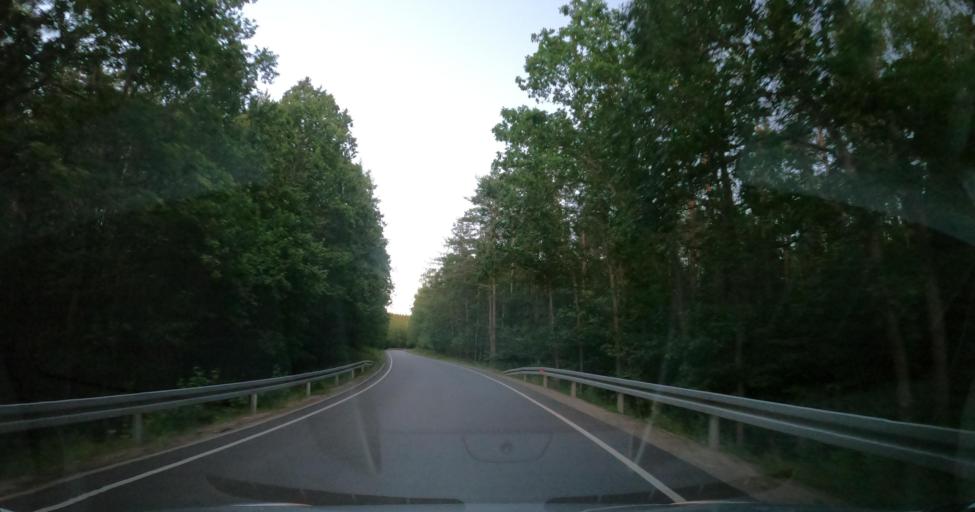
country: PL
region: Pomeranian Voivodeship
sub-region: Powiat leborski
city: Lebork
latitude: 54.5147
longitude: 17.7996
